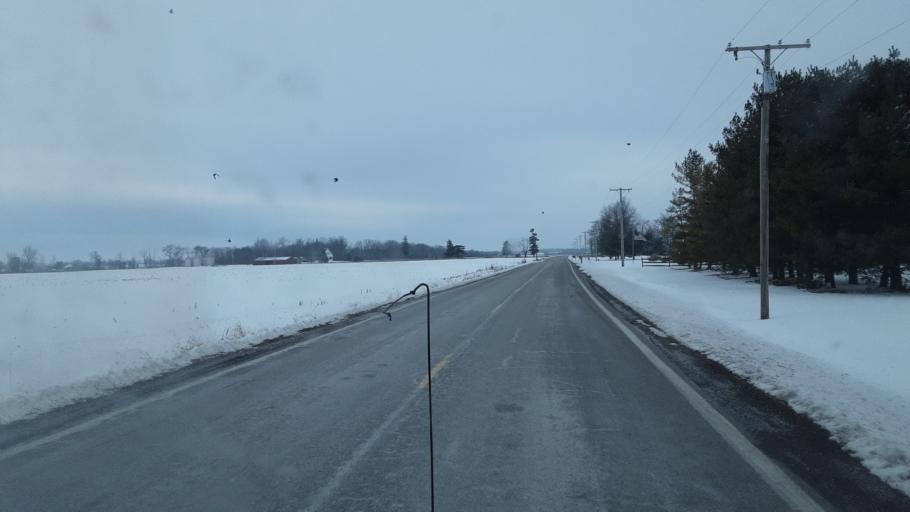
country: US
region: Ohio
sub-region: Champaign County
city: Mechanicsburg
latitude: 40.1198
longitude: -83.4630
